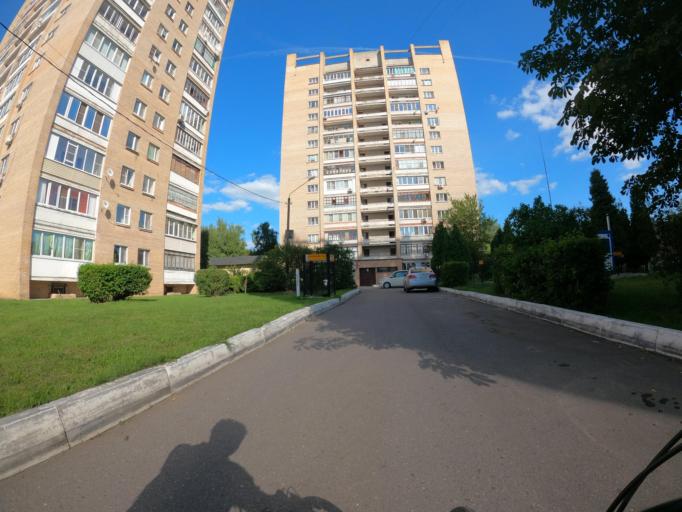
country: RU
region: Moskovskaya
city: Stupino
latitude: 54.8874
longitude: 38.0541
